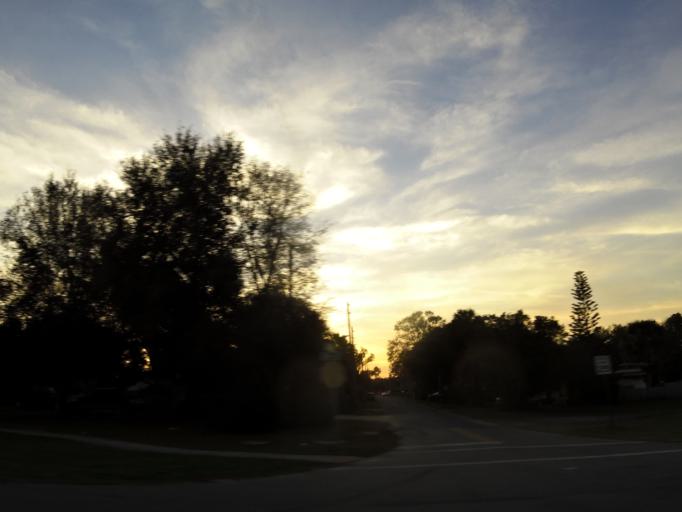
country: US
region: Florida
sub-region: Volusia County
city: North DeLand
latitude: 29.0784
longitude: -81.3049
